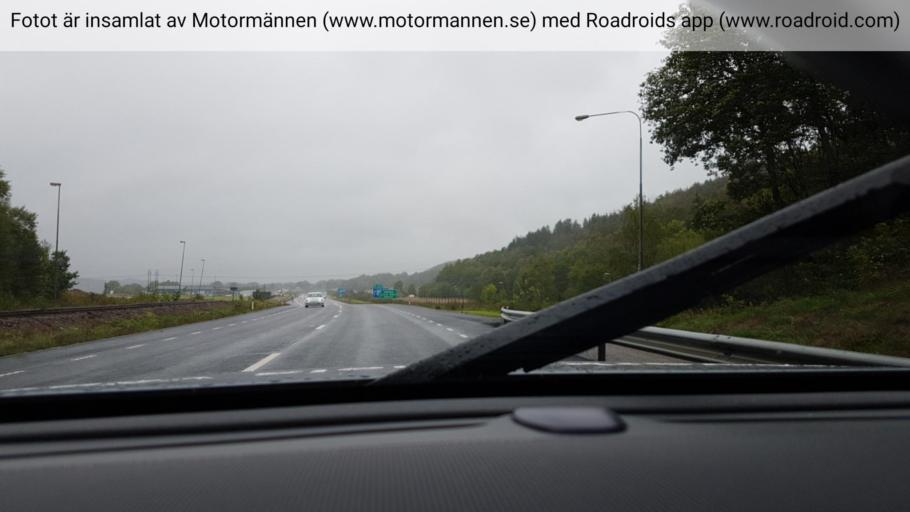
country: SE
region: Vaestra Goetaland
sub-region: Lilla Edets Kommun
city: Lilla Edet
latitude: 58.1131
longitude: 12.1430
